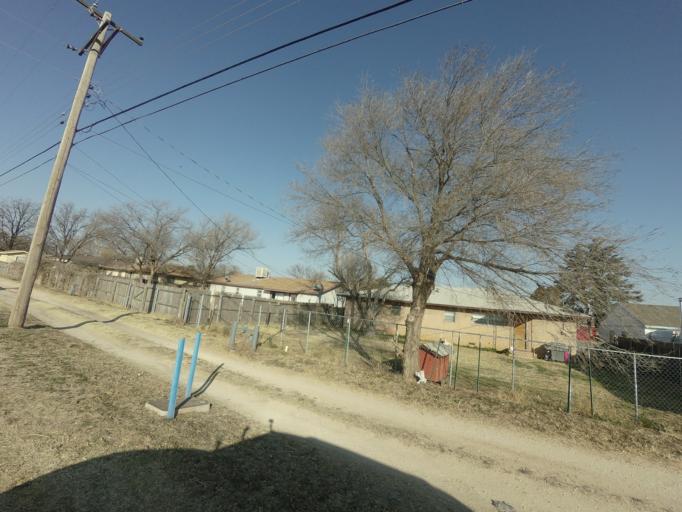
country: US
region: New Mexico
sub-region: Curry County
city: Clovis
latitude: 34.4156
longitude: -103.2106
